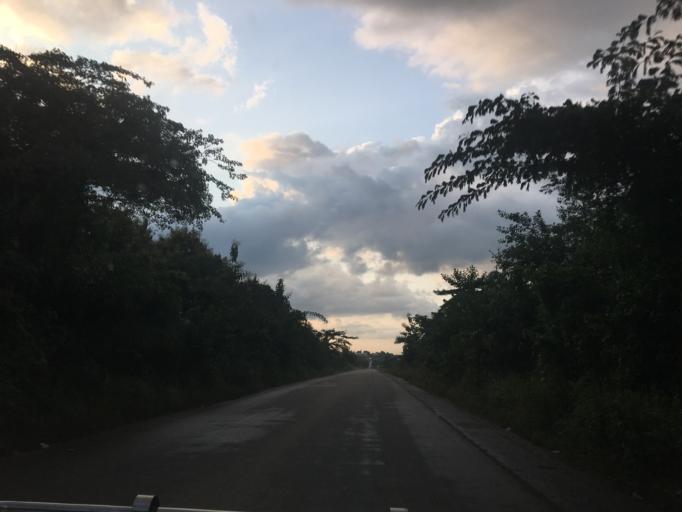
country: GH
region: Western
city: Bibiani
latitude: 6.7713
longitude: -2.5113
